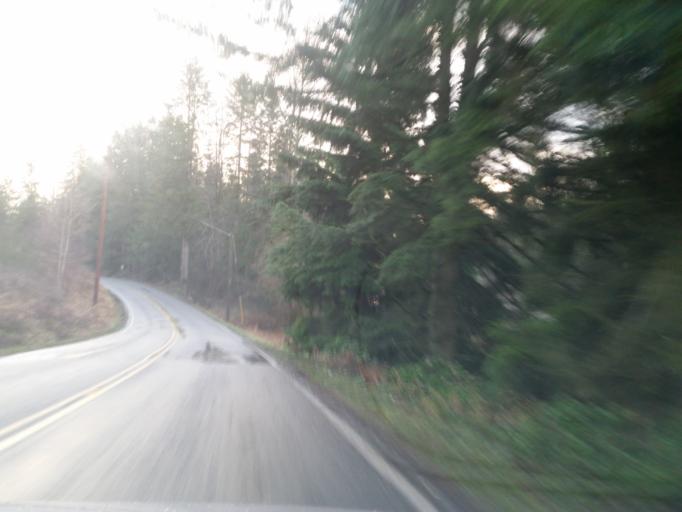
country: US
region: Washington
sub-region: Snohomish County
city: Maltby
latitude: 47.8123
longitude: -122.0984
